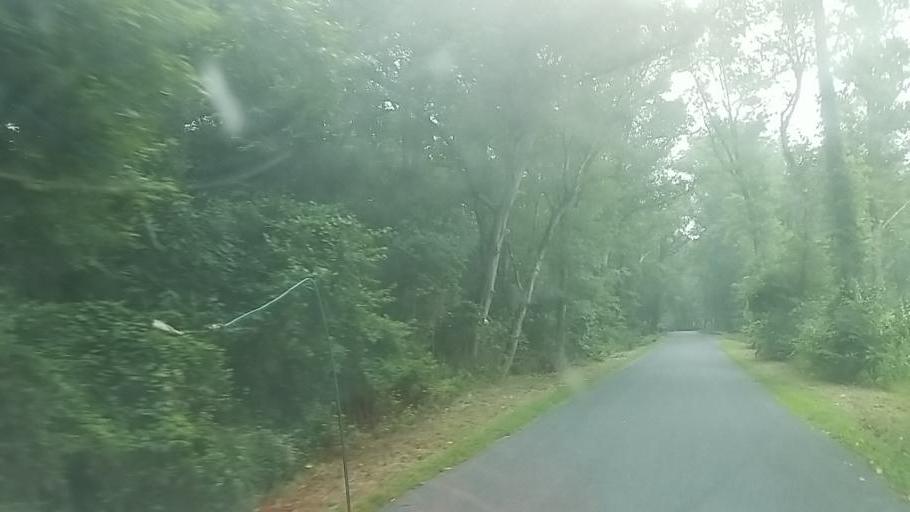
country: US
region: Maryland
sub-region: Wicomico County
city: Pittsville
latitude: 38.4412
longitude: -75.3384
